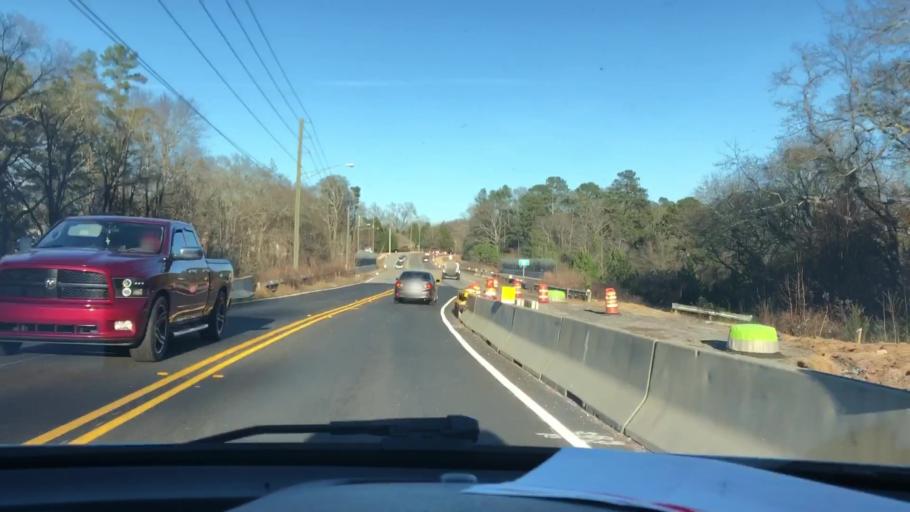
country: US
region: Georgia
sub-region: Gwinnett County
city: Mountain Park
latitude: 33.8732
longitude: -84.0849
